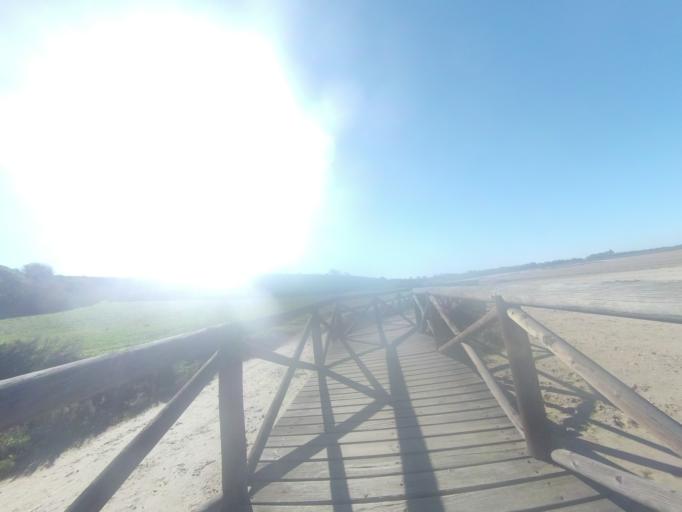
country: ES
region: Andalusia
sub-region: Provincia de Huelva
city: Palos de la Frontera
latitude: 37.2381
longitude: -6.8920
